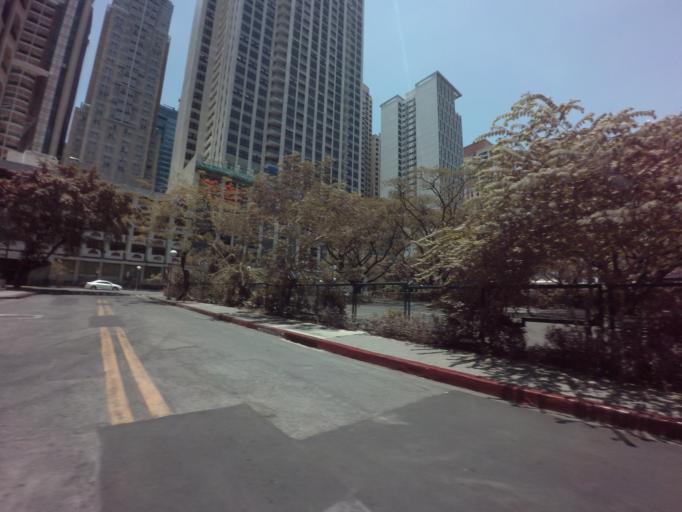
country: PH
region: Metro Manila
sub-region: Makati City
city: Makati City
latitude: 14.5601
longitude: 121.0234
